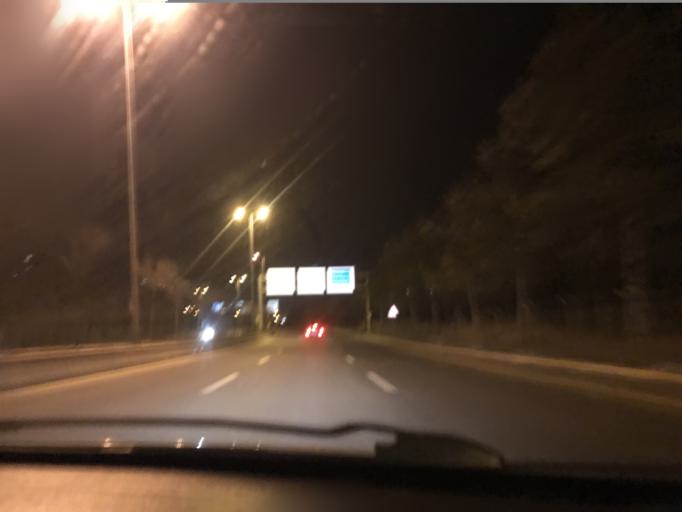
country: TR
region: Ankara
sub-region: Goelbasi
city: Golbasi
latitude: 39.8431
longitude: 32.7996
